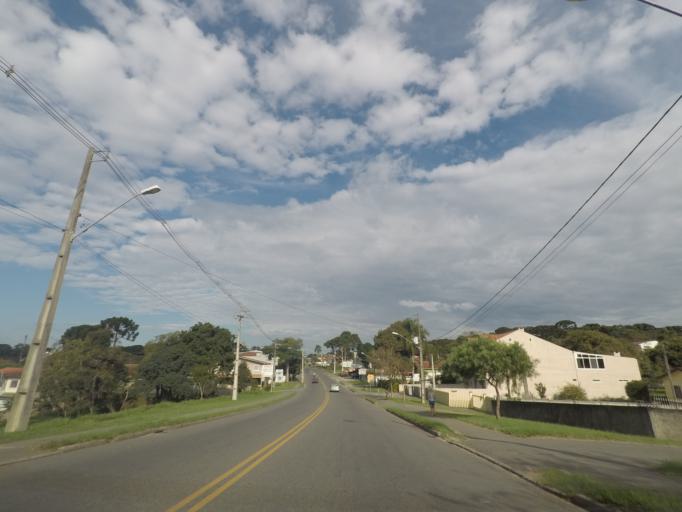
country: BR
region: Parana
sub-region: Sao Jose Dos Pinhais
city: Sao Jose dos Pinhais
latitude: -25.5639
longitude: -49.2901
